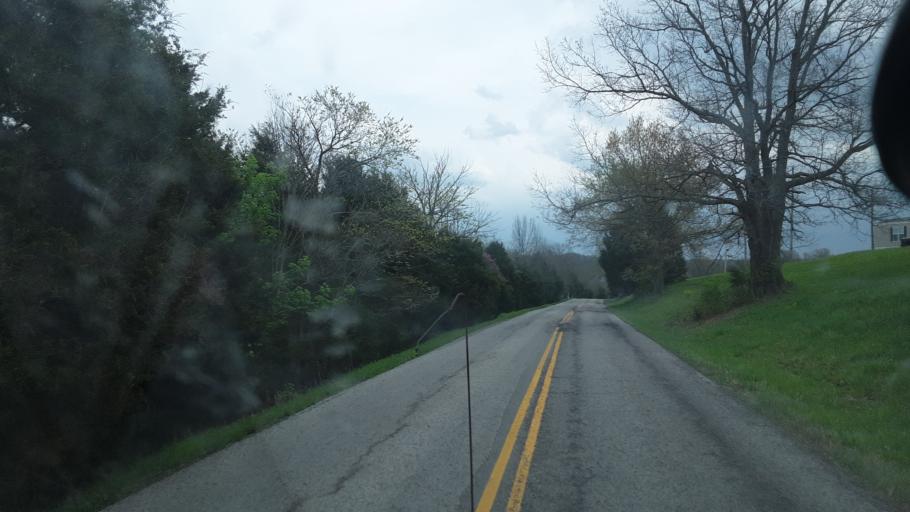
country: US
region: Kentucky
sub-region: Grant County
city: Dry Ridge
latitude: 38.6445
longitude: -84.7273
